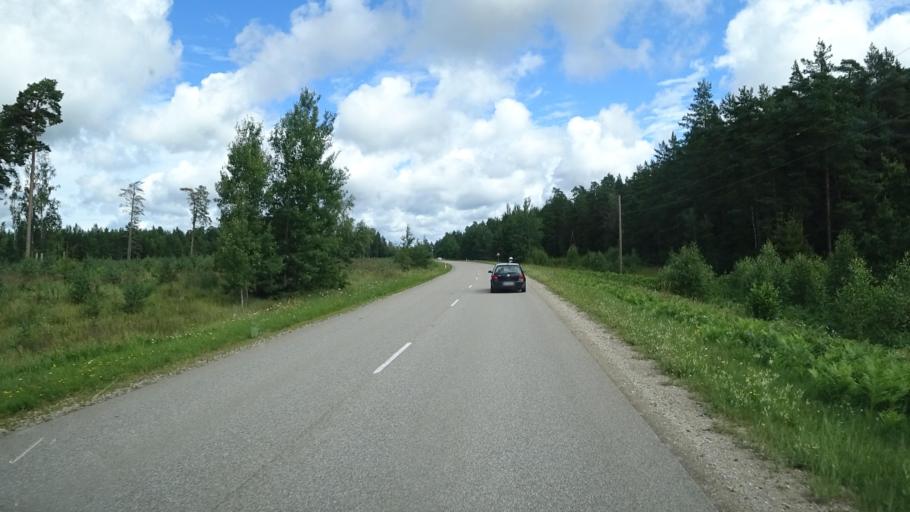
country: LV
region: Grobina
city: Grobina
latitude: 56.6923
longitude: 21.1592
